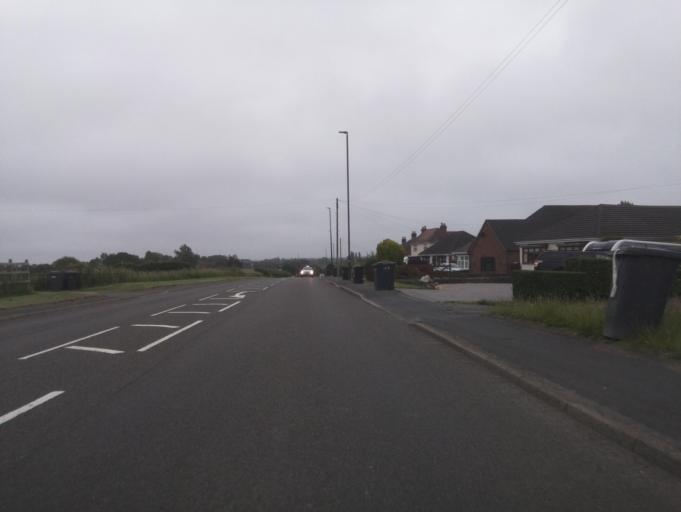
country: GB
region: England
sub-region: Derbyshire
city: Netherseal
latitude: 52.7411
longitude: -1.5711
